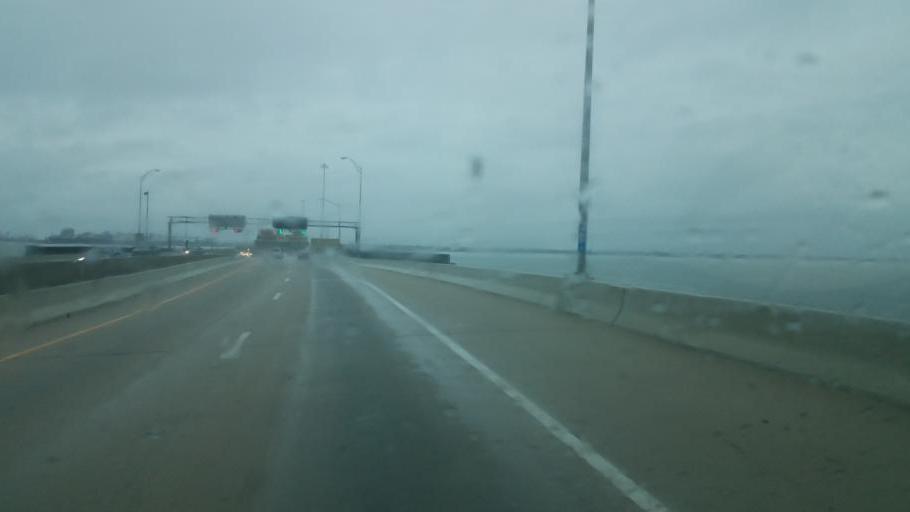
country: US
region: Virginia
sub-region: City of Newport News
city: Newport News
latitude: 36.9427
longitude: -76.4026
